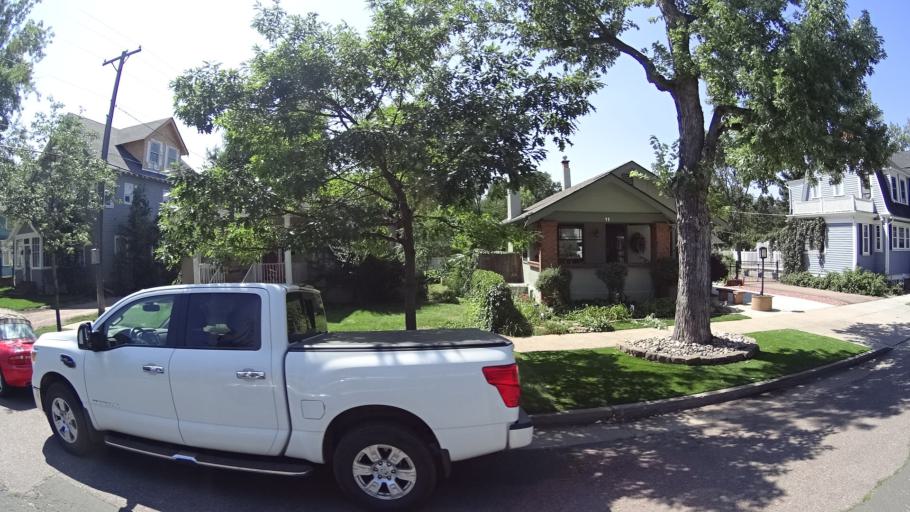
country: US
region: Colorado
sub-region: El Paso County
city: Colorado Springs
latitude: 38.8592
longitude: -104.8236
